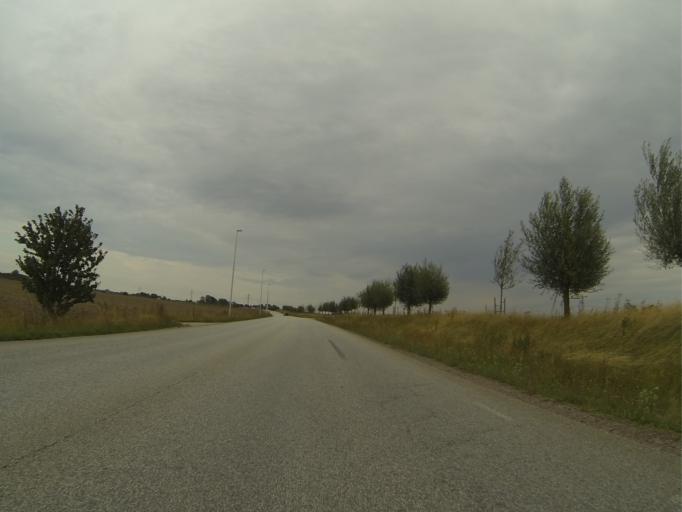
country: SE
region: Skane
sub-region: Burlovs Kommun
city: Arloev
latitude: 55.6313
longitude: 13.1019
